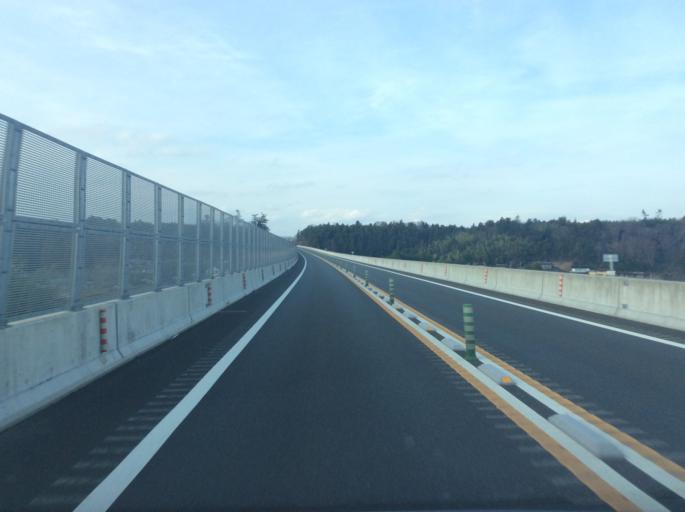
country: JP
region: Fukushima
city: Namie
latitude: 37.4749
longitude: 140.9601
